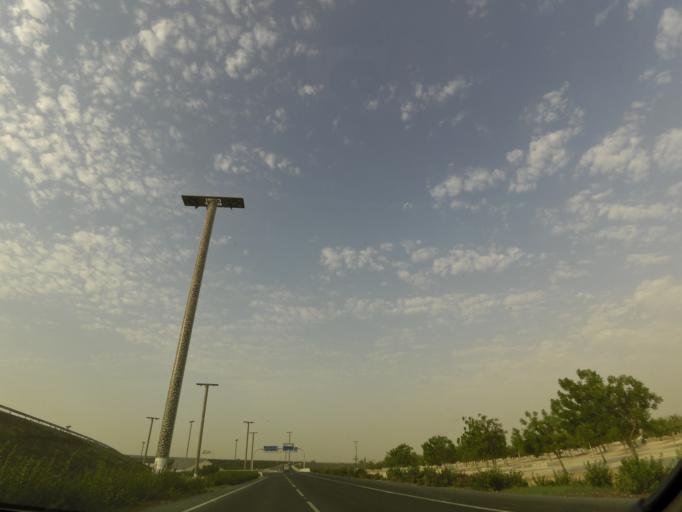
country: QA
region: Al Wakrah
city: Al Wakrah
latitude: 25.2416
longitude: 51.5896
